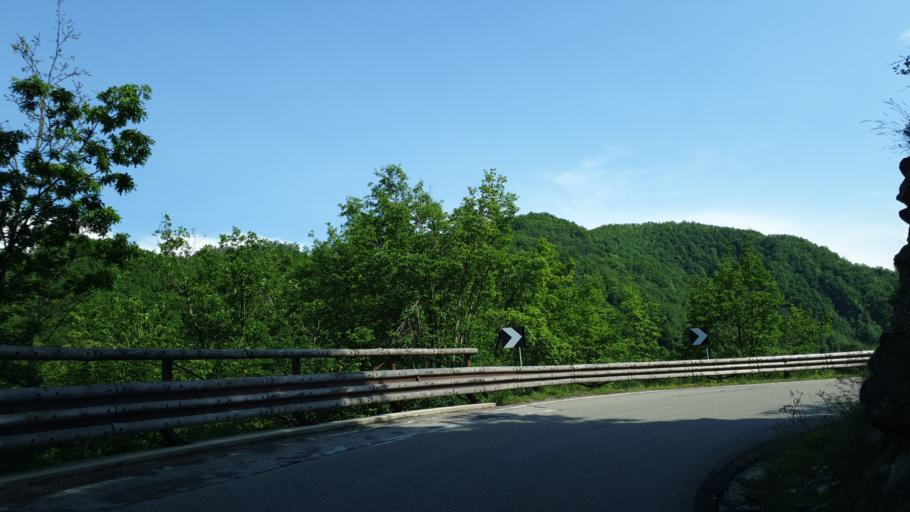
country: IT
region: Emilia-Romagna
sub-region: Forli-Cesena
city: San Piero in Bagno
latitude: 43.8192
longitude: 11.9544
